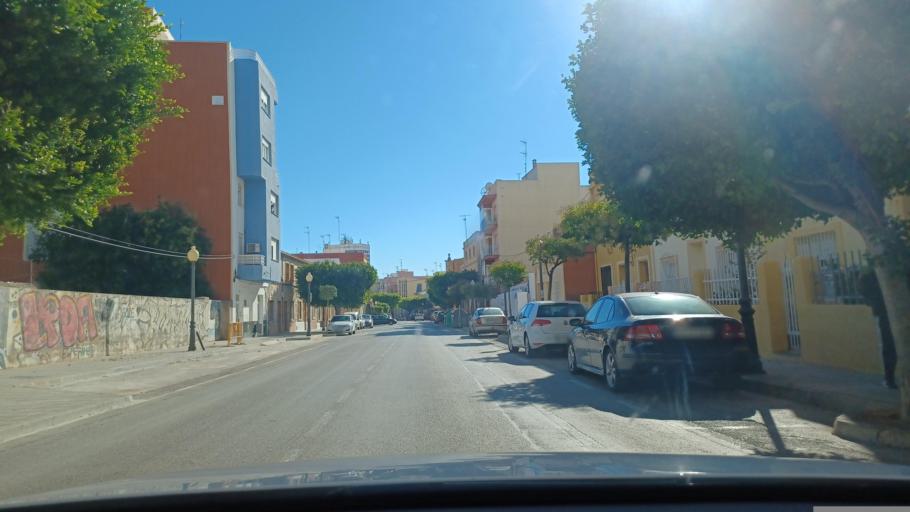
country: ES
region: Valencia
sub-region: Provincia de Castello
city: Benicarlo
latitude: 40.4211
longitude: 0.4196
